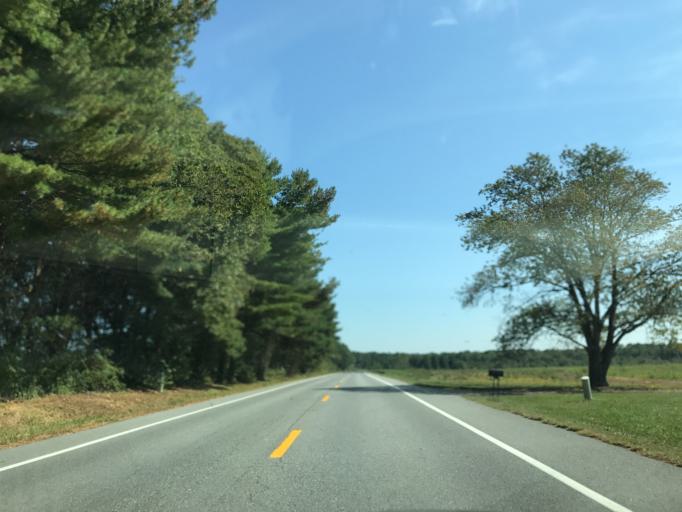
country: US
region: Delaware
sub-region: New Castle County
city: Townsend
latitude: 39.3037
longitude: -75.8006
